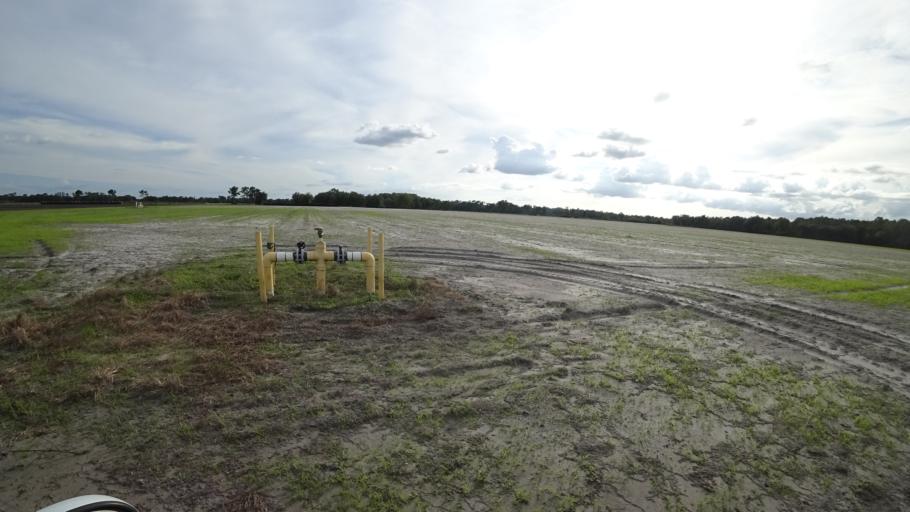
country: US
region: Florida
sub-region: Hillsborough County
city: Wimauma
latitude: 27.5615
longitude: -82.0961
